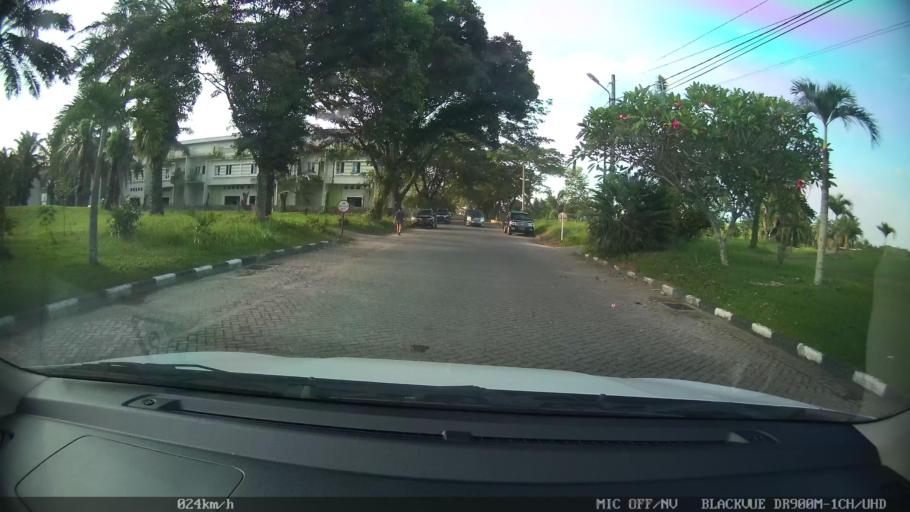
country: ID
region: North Sumatra
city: Medan
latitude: 3.6220
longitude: 98.6431
